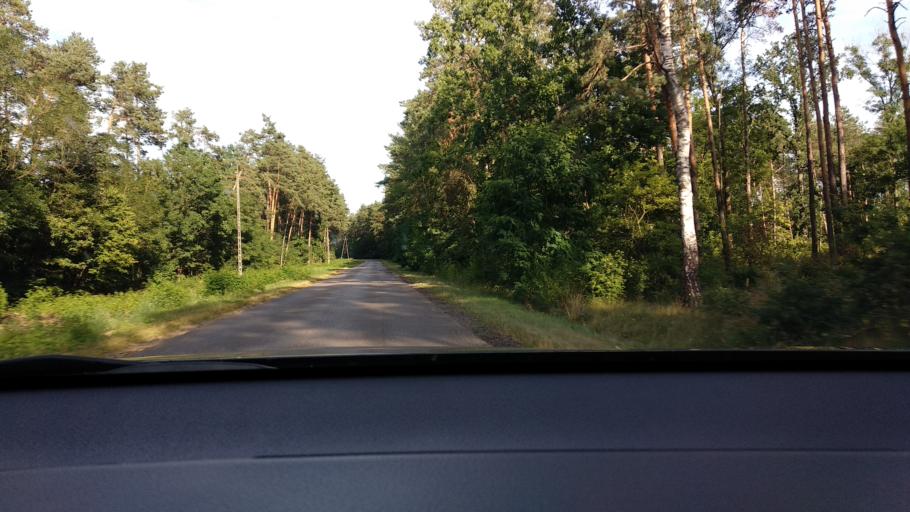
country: PL
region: Masovian Voivodeship
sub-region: Powiat pultuski
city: Pultusk
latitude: 52.7129
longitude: 21.1560
